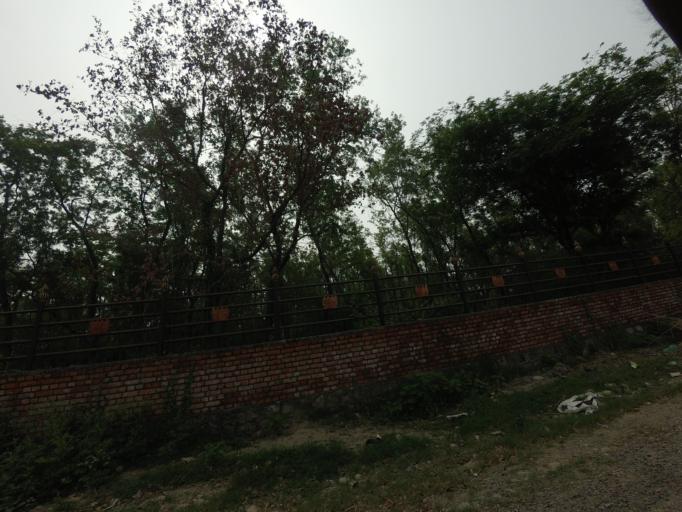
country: IN
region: Uttar Pradesh
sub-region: Maharajganj
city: Nautanwa
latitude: 27.4892
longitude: 83.2681
